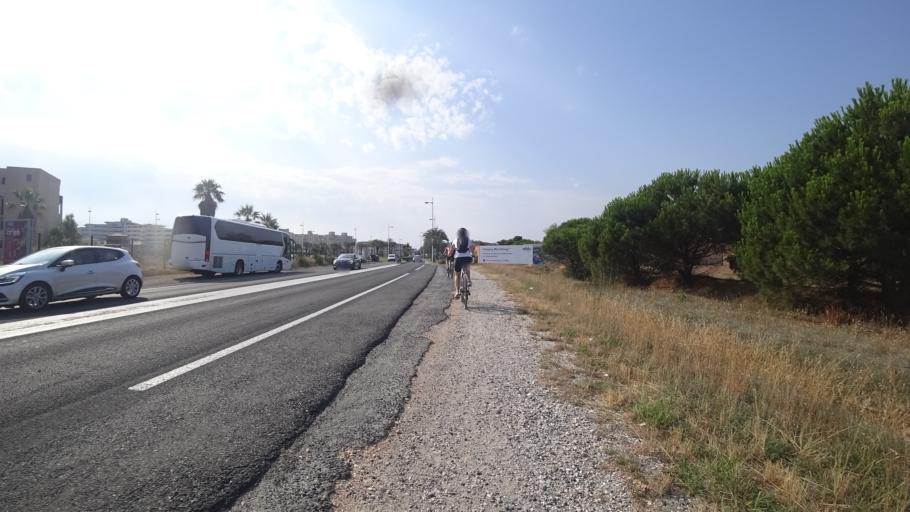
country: FR
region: Languedoc-Roussillon
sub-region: Departement des Pyrenees-Orientales
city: Canet-en-Roussillon
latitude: 42.6779
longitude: 3.0296
